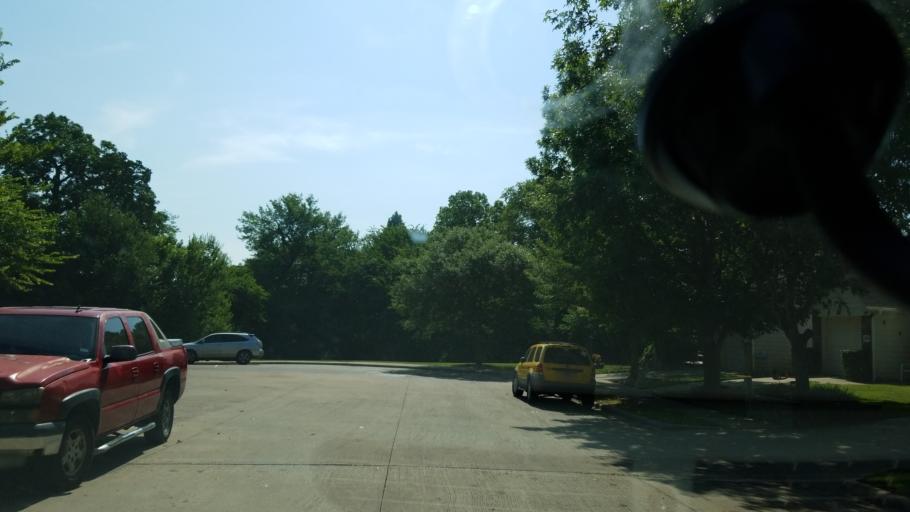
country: US
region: Texas
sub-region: Dallas County
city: Cockrell Hill
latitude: 32.7087
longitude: -96.8686
